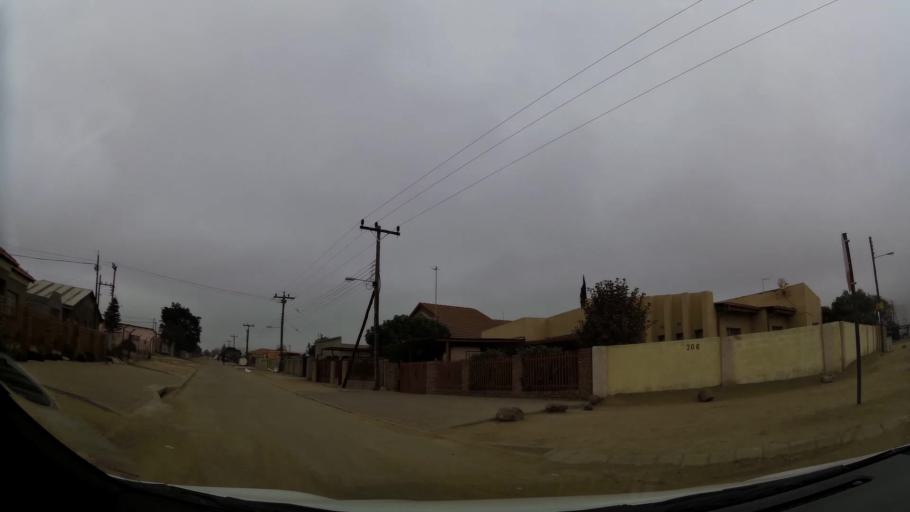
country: ZA
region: Limpopo
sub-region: Capricorn District Municipality
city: Polokwane
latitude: -23.8349
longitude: 29.3883
